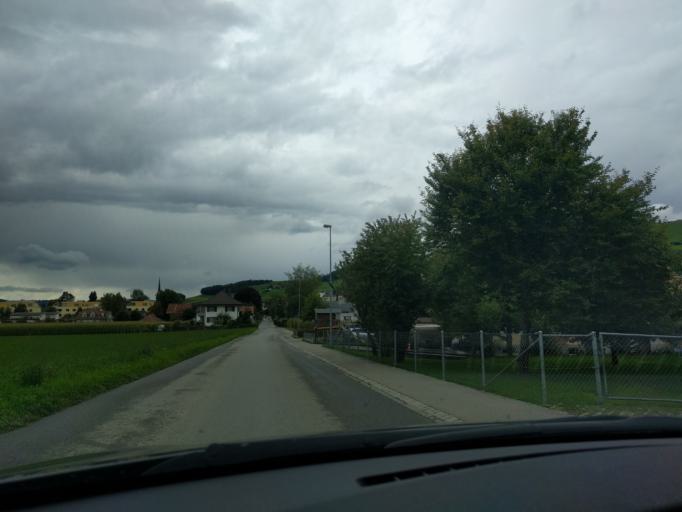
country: CH
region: Bern
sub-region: Bern-Mittelland District
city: Konolfingen
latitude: 46.8778
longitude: 7.6287
